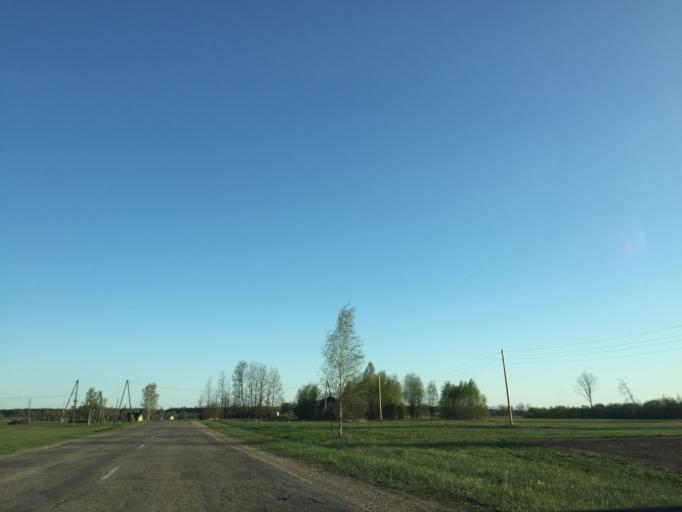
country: LV
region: Koknese
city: Koknese
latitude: 56.6870
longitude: 25.4869
